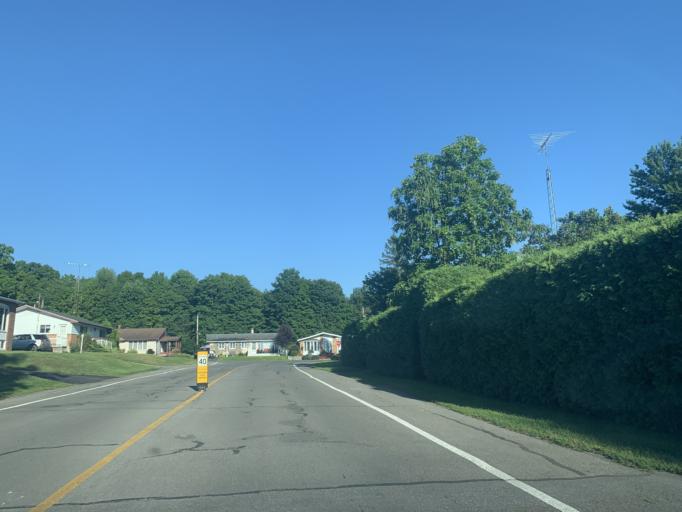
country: CA
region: Ontario
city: Hawkesbury
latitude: 45.6286
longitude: -74.5987
